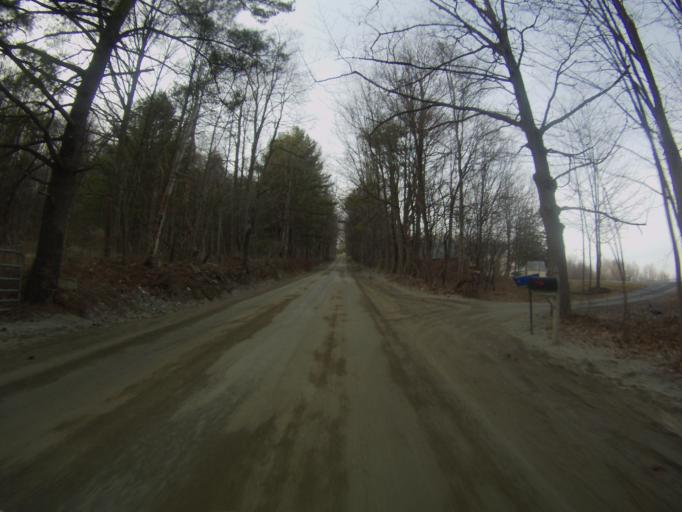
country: US
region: Vermont
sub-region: Addison County
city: Middlebury (village)
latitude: 44.0227
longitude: -73.2587
